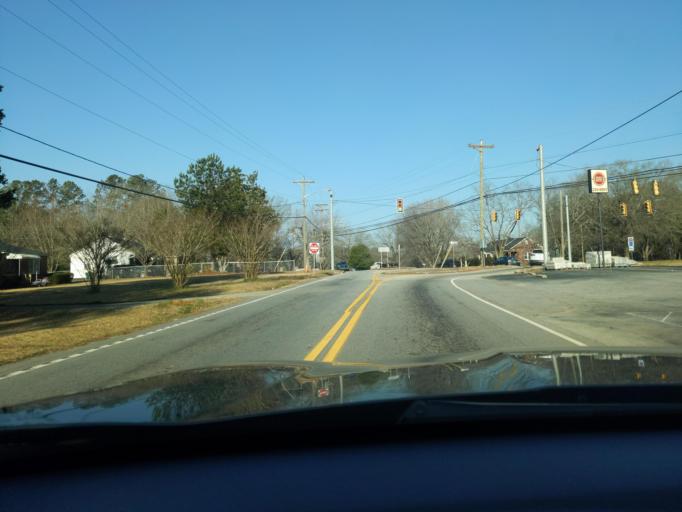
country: US
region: South Carolina
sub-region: Greenwood County
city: Greenwood
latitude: 34.1951
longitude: -82.1302
